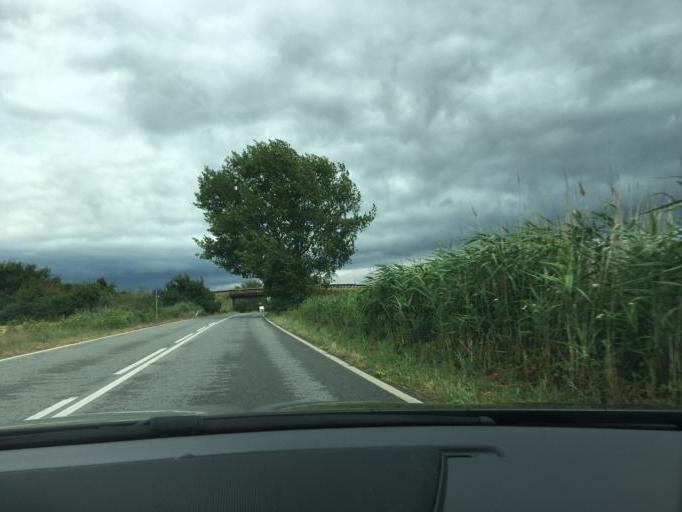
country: BG
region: Kyustendil
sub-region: Obshtina Dupnitsa
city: Dupnitsa
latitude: 42.2722
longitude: 23.0313
